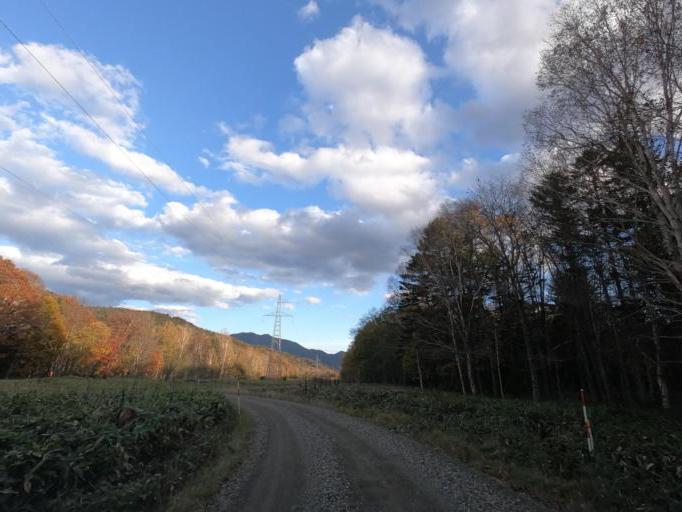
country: JP
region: Hokkaido
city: Otofuke
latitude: 43.4321
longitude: 143.1603
